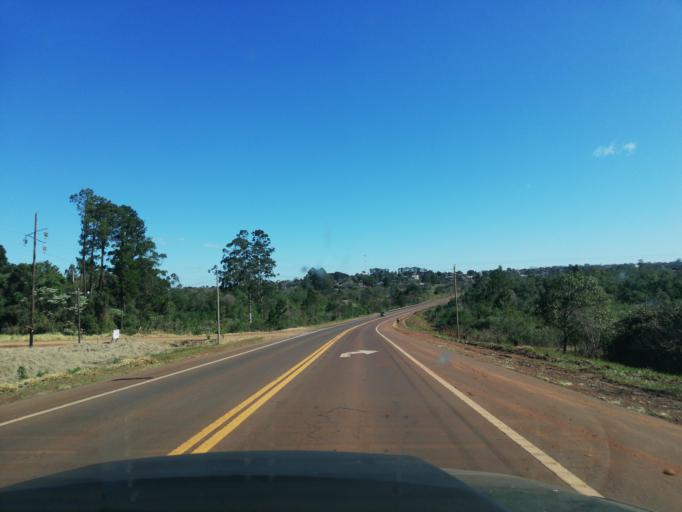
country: AR
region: Misiones
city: Aristobulo del Valle
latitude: -27.0975
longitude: -54.8744
